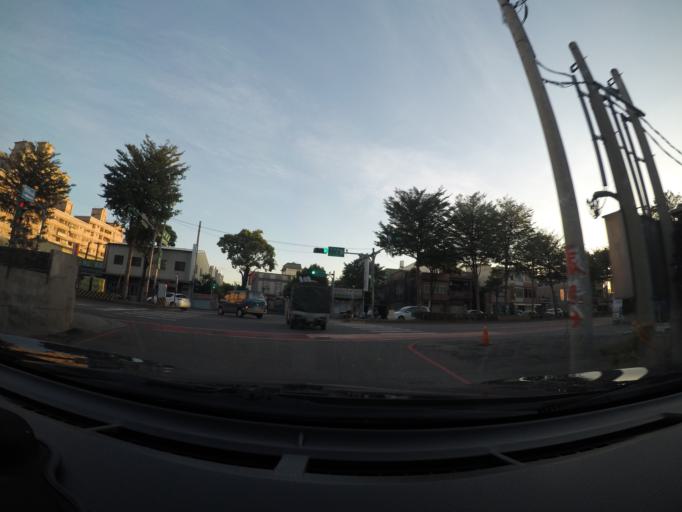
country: TW
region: Taiwan
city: Taoyuan City
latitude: 24.9931
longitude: 121.2739
